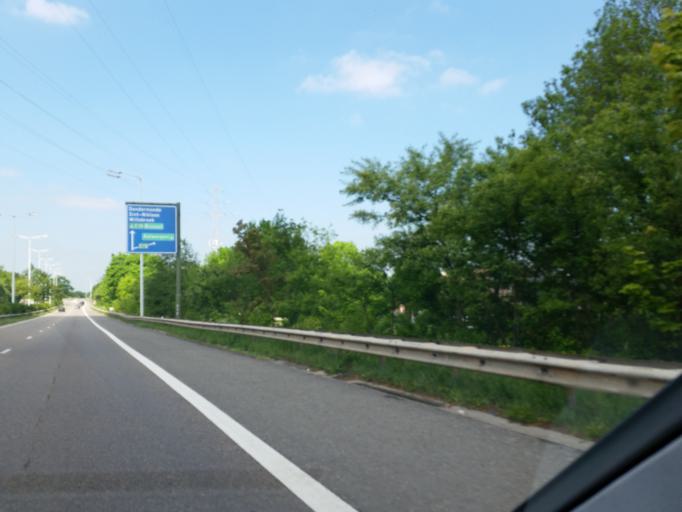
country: BE
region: Flanders
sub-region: Provincie Antwerpen
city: Mechelen
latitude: 51.0392
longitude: 4.4638
